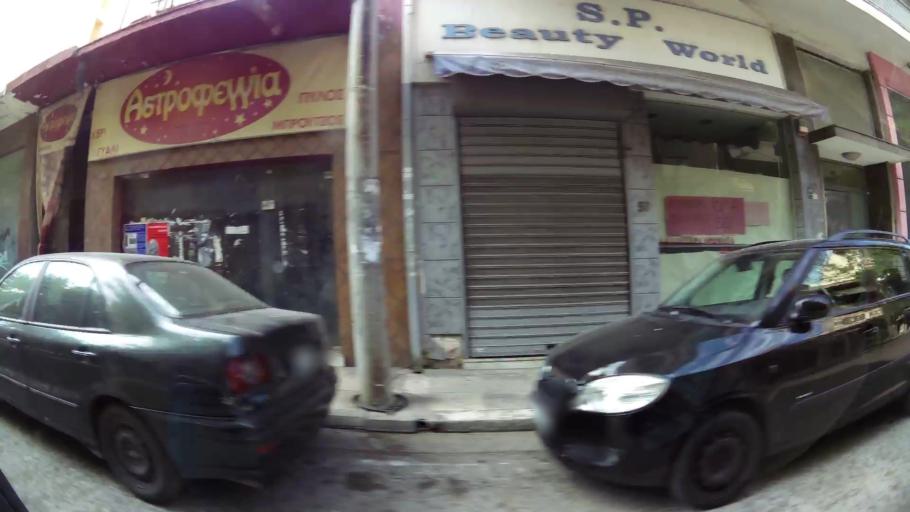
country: GR
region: Attica
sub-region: Nomarchia Athinas
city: Athens
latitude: 37.9883
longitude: 23.7123
